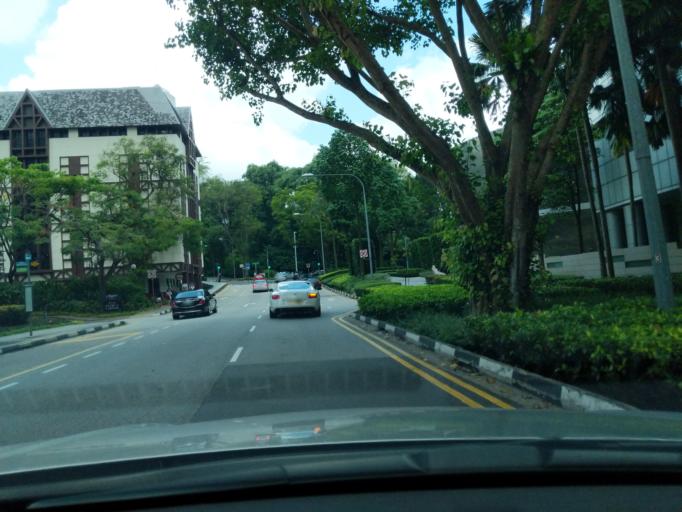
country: SG
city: Singapore
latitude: 1.3049
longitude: 103.8256
